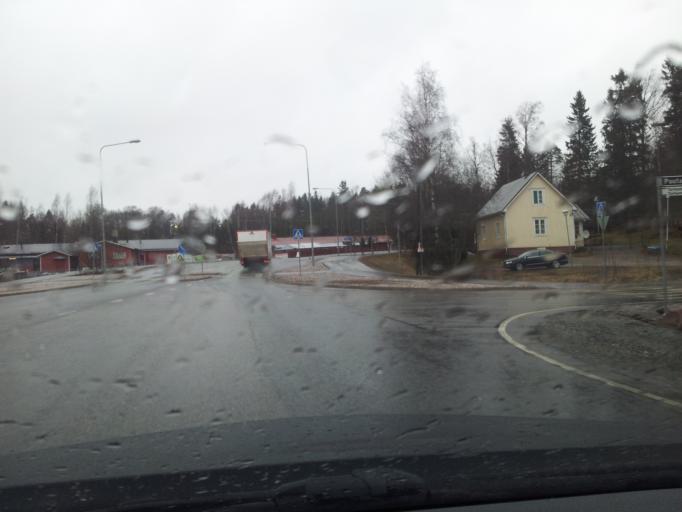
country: FI
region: Uusimaa
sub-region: Helsinki
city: Kirkkonummi
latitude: 60.1348
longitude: 24.5096
